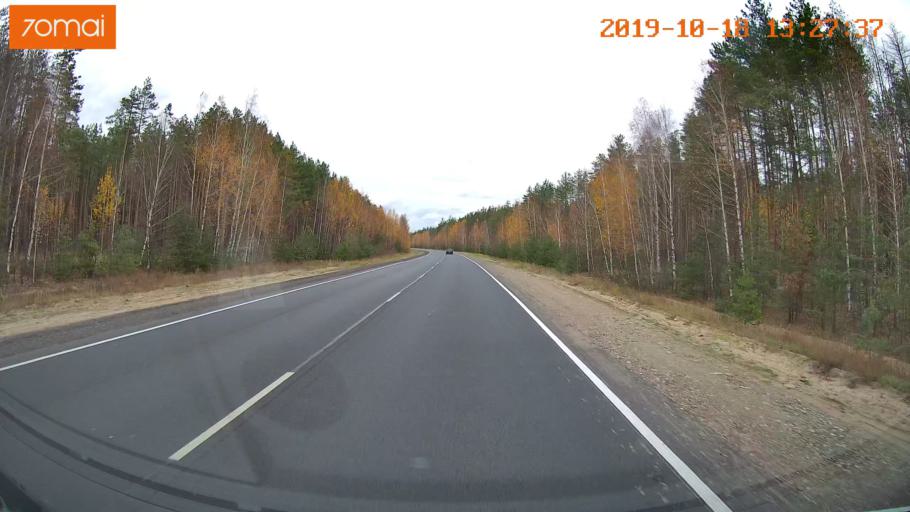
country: RU
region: Rjazan
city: Solotcha
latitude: 54.7663
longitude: 39.8573
